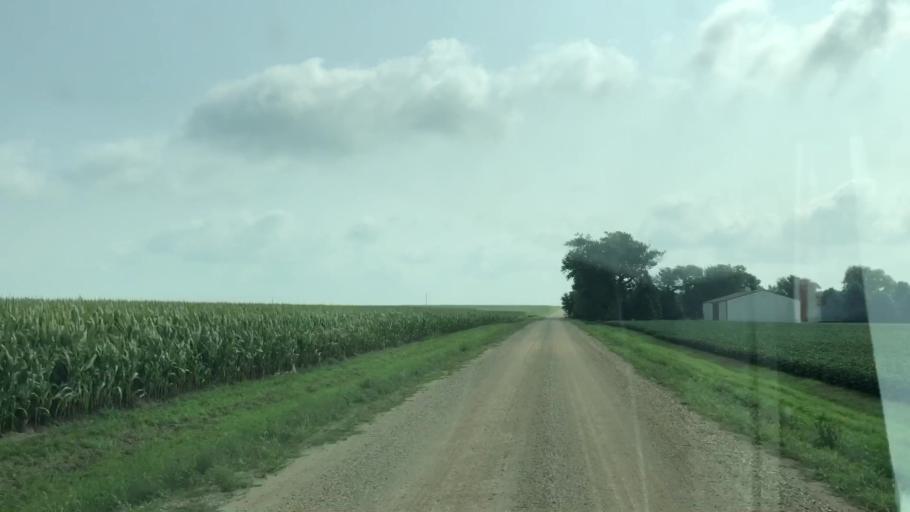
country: US
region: Iowa
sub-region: O'Brien County
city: Sheldon
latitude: 43.2153
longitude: -95.9459
